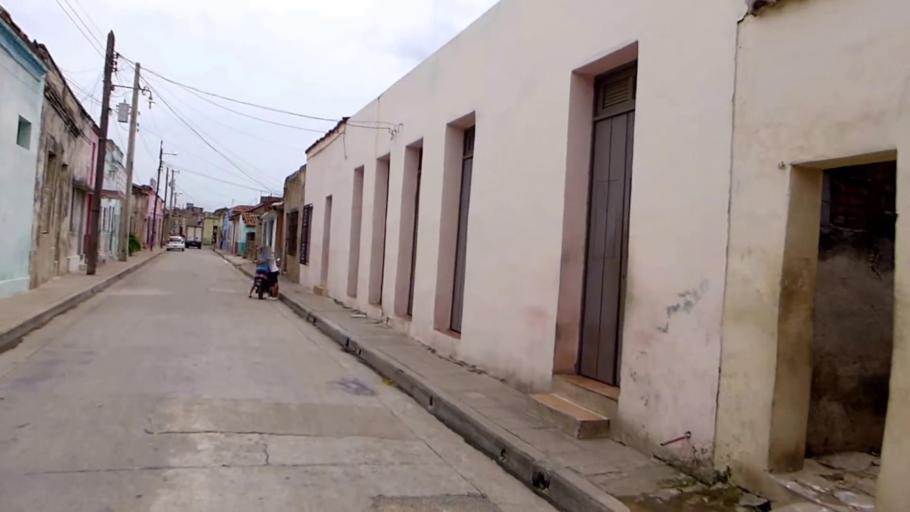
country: CU
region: Camaguey
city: Camaguey
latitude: 21.3795
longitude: -77.9219
